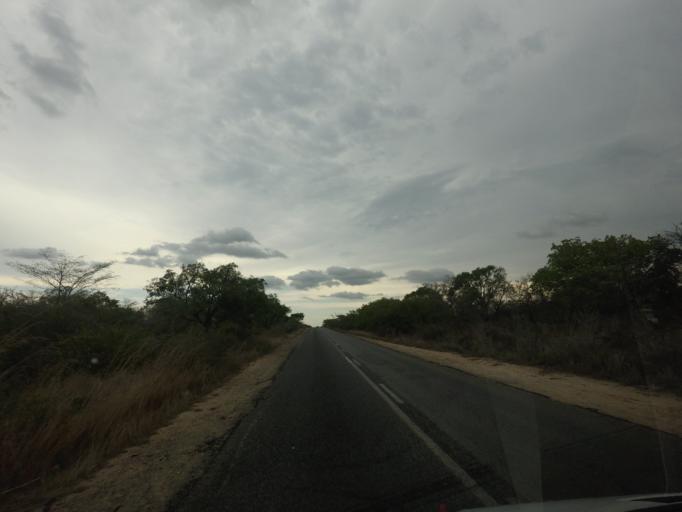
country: ZA
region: Limpopo
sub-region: Mopani District Municipality
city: Hoedspruit
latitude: -24.5333
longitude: 30.9996
